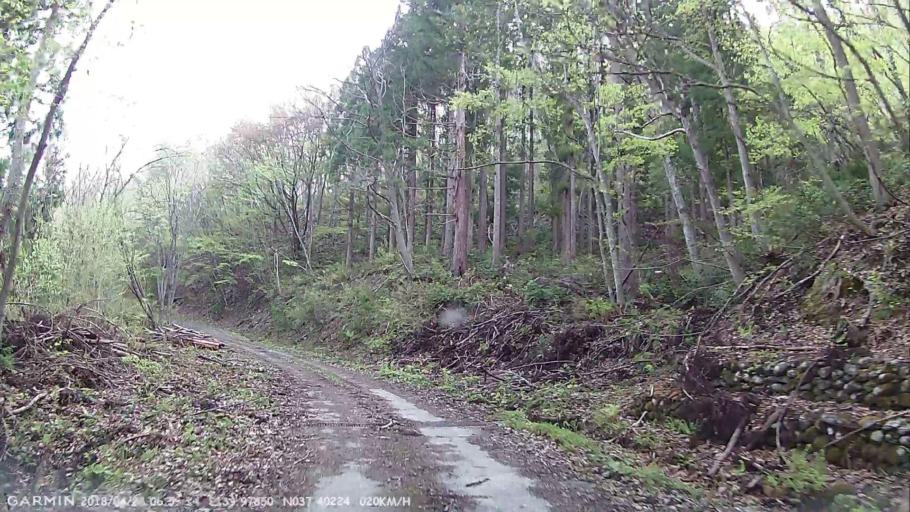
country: JP
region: Fukushima
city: Inawashiro
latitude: 37.4023
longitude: 139.9785
